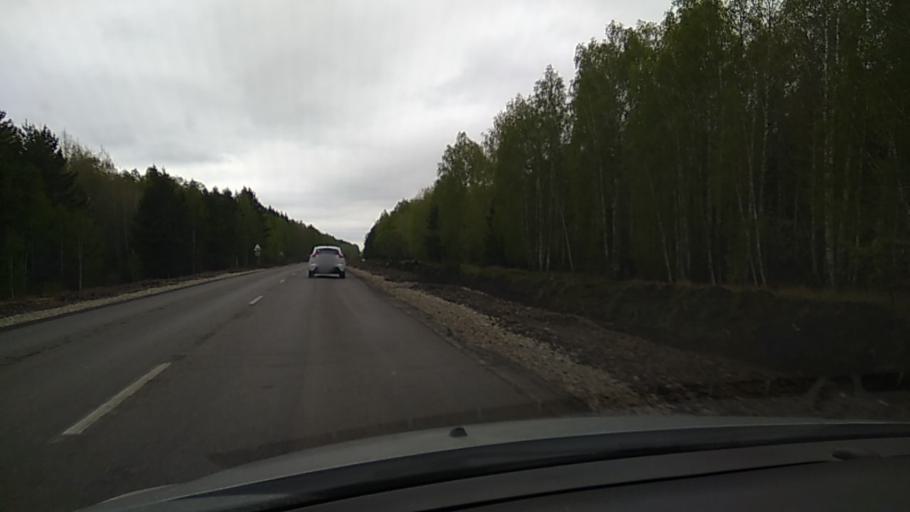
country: RU
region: Kurgan
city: Shadrinsk
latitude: 56.1421
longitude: 63.5150
